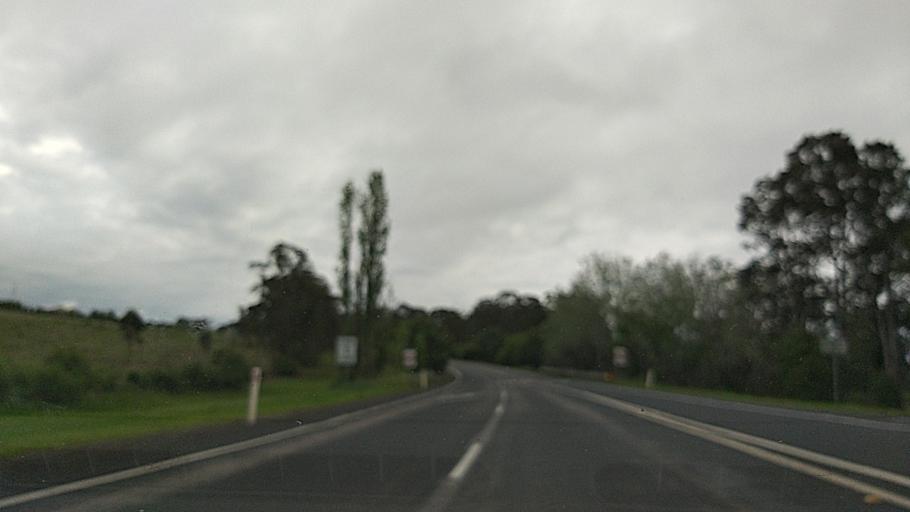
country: AU
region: New South Wales
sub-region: Camden
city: Camden South
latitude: -34.1210
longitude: 150.6989
